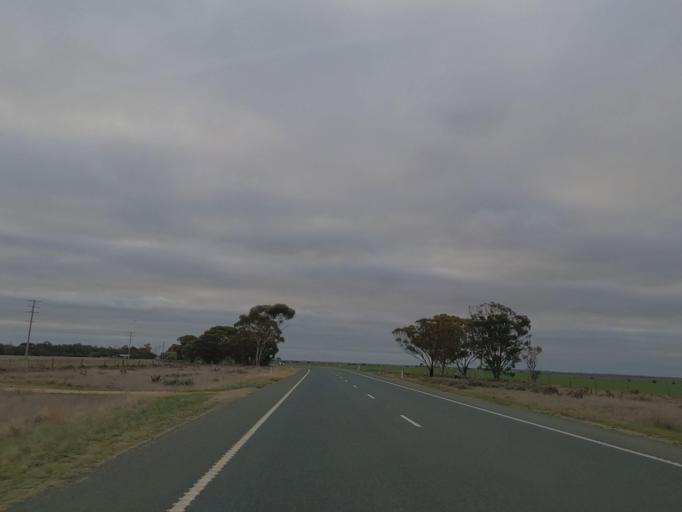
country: AU
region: Victoria
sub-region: Swan Hill
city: Swan Hill
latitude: -35.5642
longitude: 143.7832
